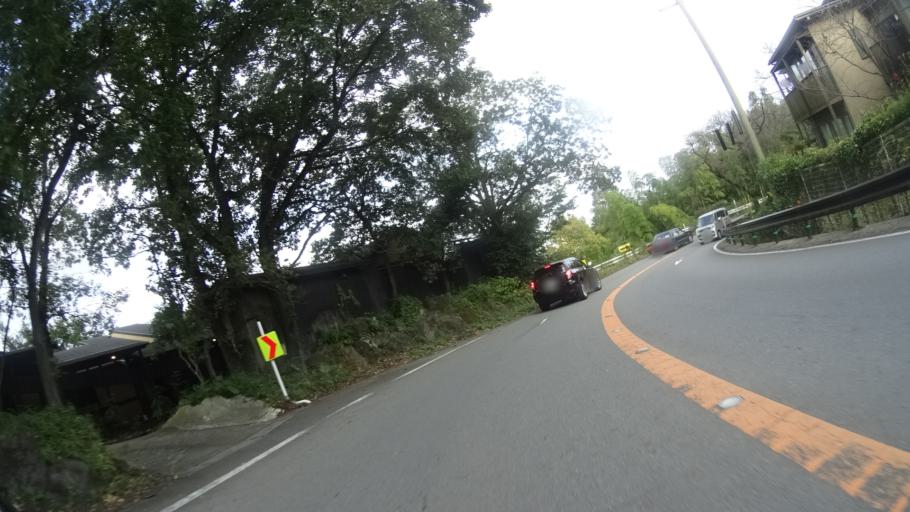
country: JP
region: Oita
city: Beppu
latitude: 33.2909
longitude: 131.4565
